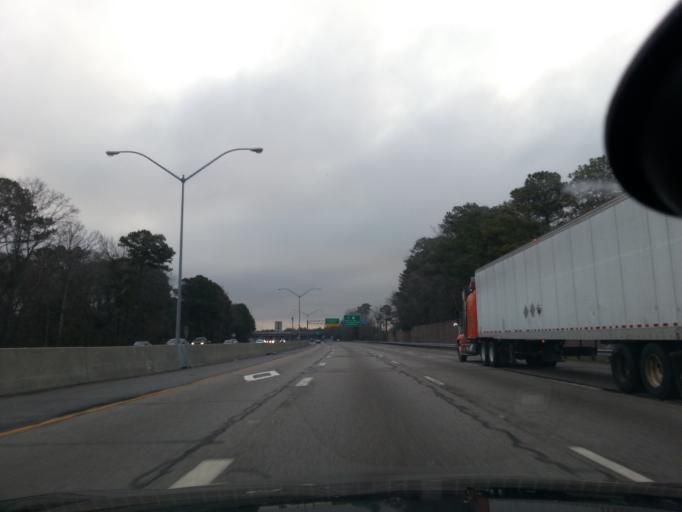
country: US
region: Virginia
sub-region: City of Chesapeake
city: Chesapeake
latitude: 36.8419
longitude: -76.2190
